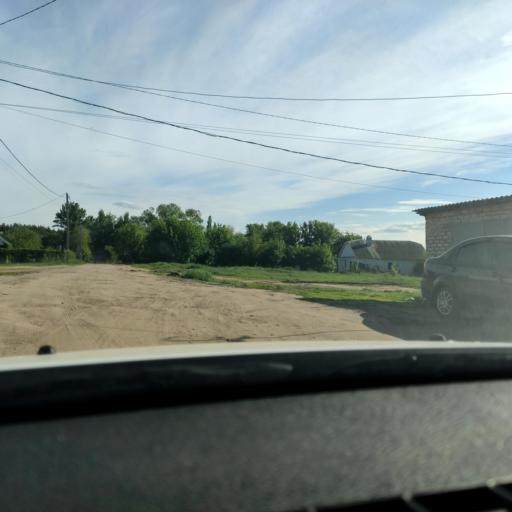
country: RU
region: Voronezj
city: Ramon'
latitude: 51.9401
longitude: 39.2053
